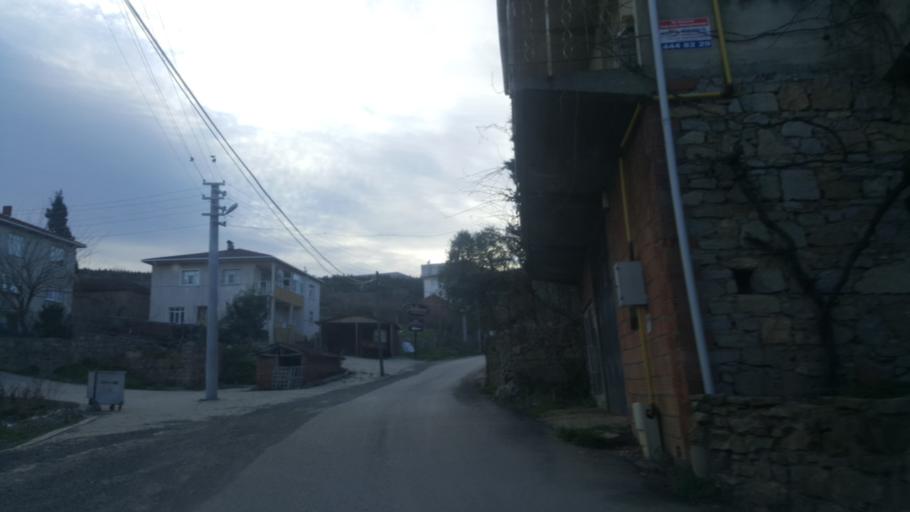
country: TR
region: Kocaeli
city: Tavsanli
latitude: 40.8454
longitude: 29.5547
